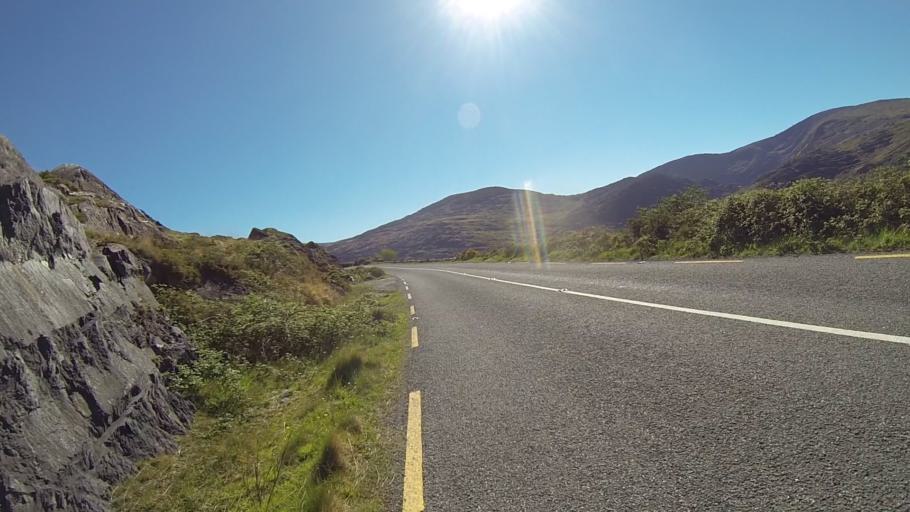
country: IE
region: Munster
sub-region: Ciarrai
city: Kenmare
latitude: 51.7719
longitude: -9.7445
